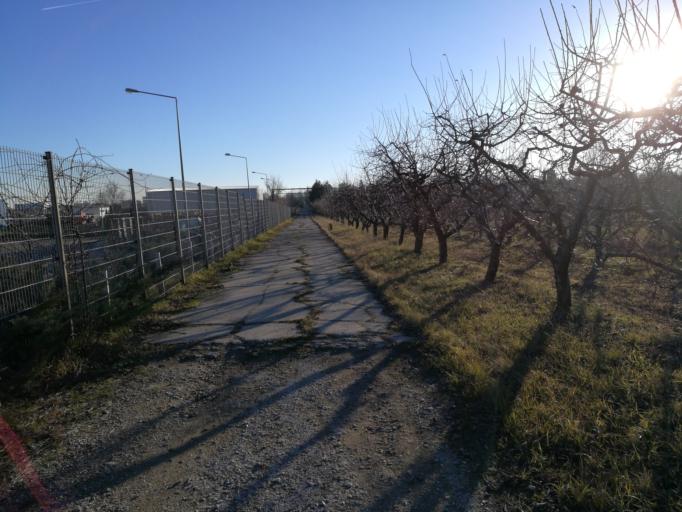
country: RO
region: Ilfov
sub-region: Comuna Otopeni
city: Otopeni
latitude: 44.5034
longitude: 26.0772
